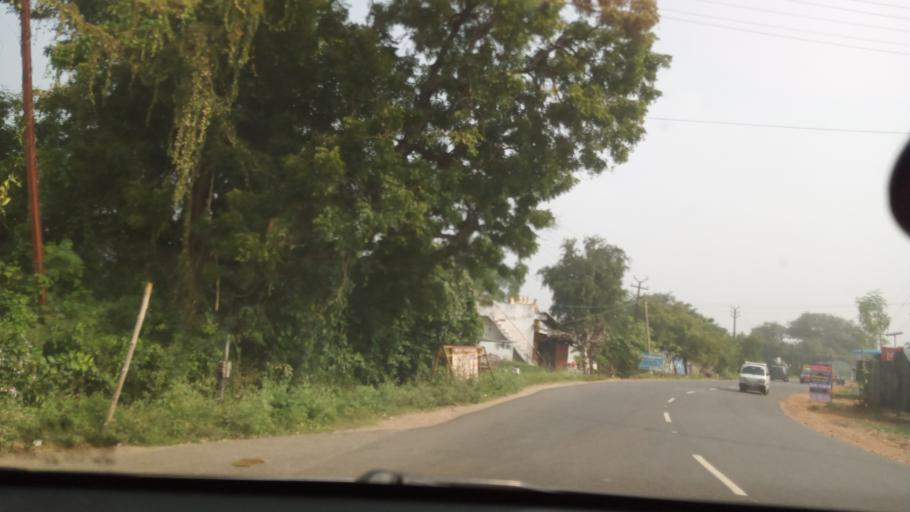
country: IN
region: Tamil Nadu
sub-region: Erode
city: Punjai Puliyampatti
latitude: 11.3272
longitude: 77.1494
